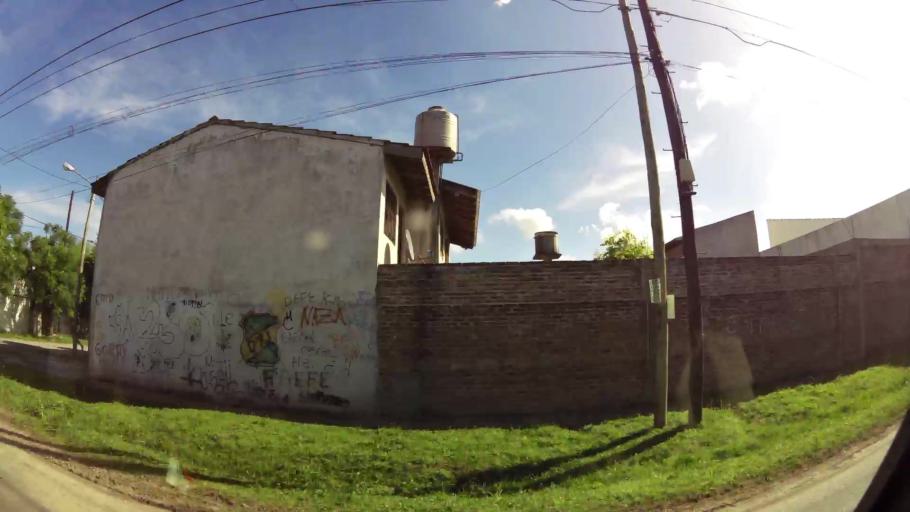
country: AR
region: Buenos Aires
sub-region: Partido de Quilmes
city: Quilmes
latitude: -34.8014
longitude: -58.2332
